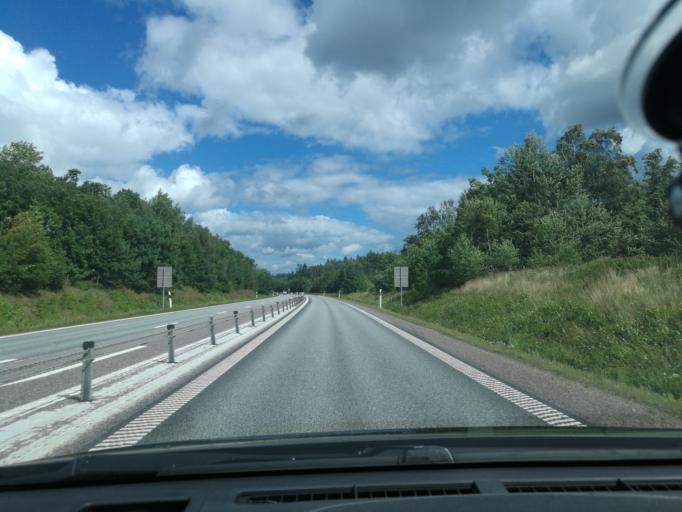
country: SE
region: Skane
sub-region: Hassleholms Kommun
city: Hastveda
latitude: 56.2523
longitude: 13.9308
